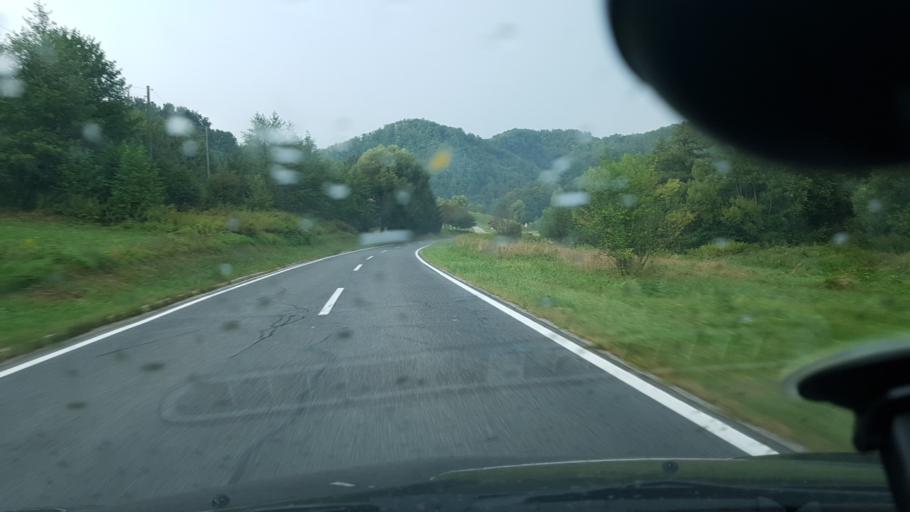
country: HR
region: Krapinsko-Zagorska
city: Pregrada
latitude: 46.2135
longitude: 15.7506
